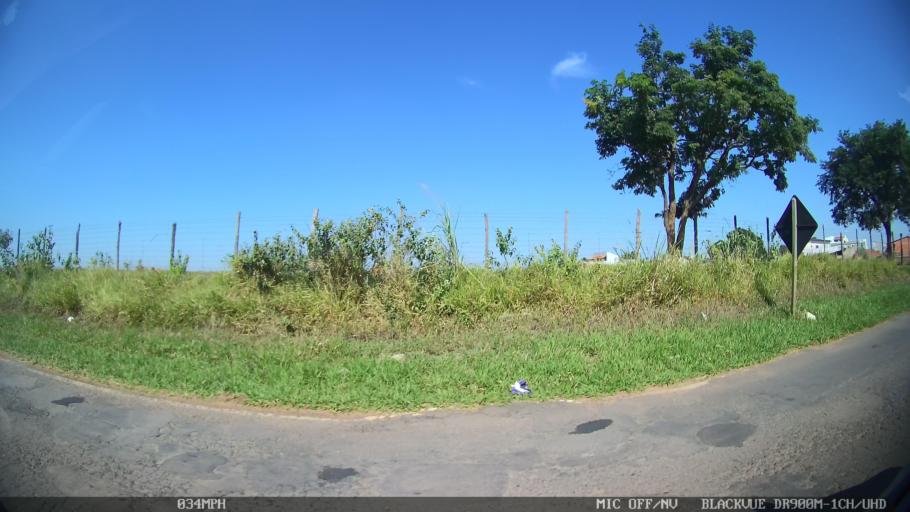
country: BR
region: Sao Paulo
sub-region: Valinhos
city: Valinhos
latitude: -23.0322
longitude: -47.1014
